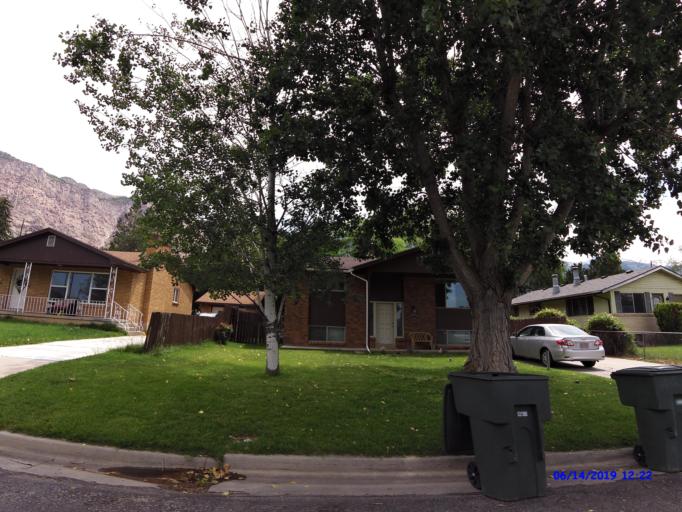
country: US
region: Utah
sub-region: Weber County
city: Ogden
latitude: 41.2536
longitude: -111.9493
